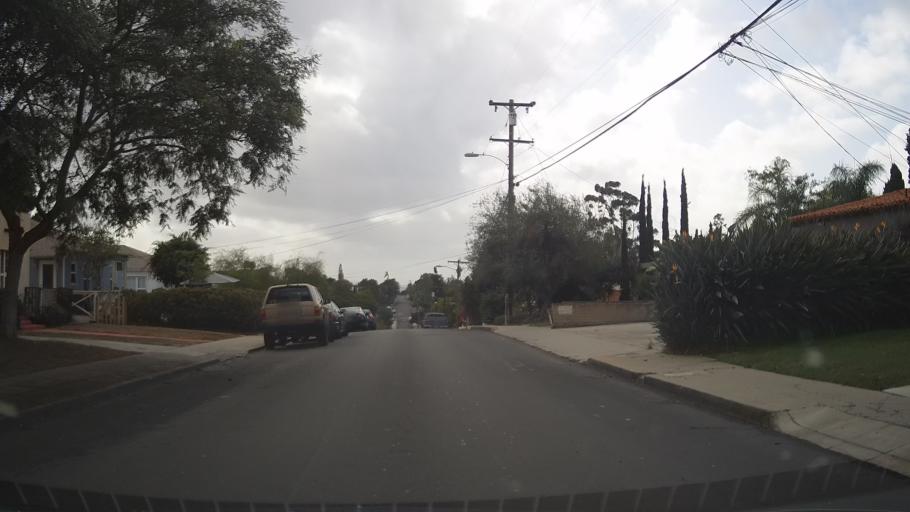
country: US
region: California
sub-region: San Diego County
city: San Diego
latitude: 32.7258
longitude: -117.1276
